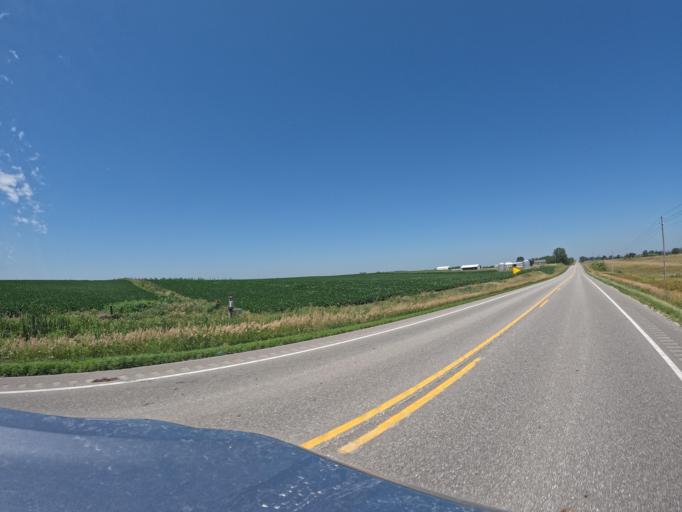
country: US
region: Iowa
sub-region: Keokuk County
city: Sigourney
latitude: 41.4558
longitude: -92.3551
